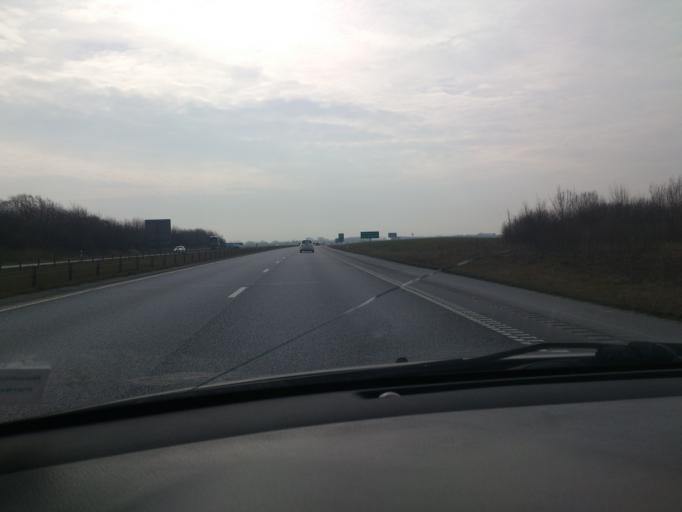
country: SE
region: Skane
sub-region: Burlovs Kommun
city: Arloev
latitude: 55.6023
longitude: 13.1169
